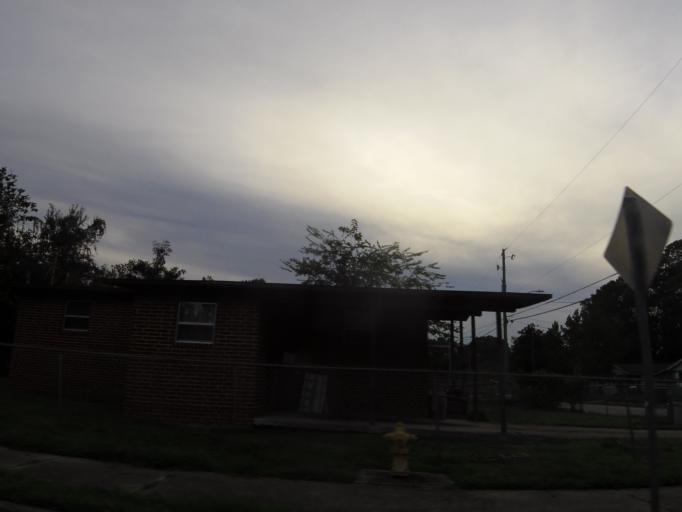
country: US
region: Florida
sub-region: Duval County
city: Jacksonville
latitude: 30.3484
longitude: -81.6986
